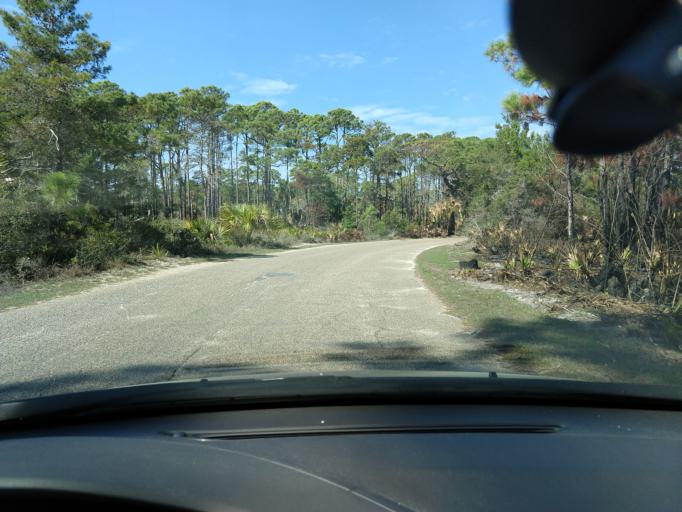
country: US
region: Florida
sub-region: Gulf County
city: Port Saint Joe
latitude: 29.7792
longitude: -85.4045
